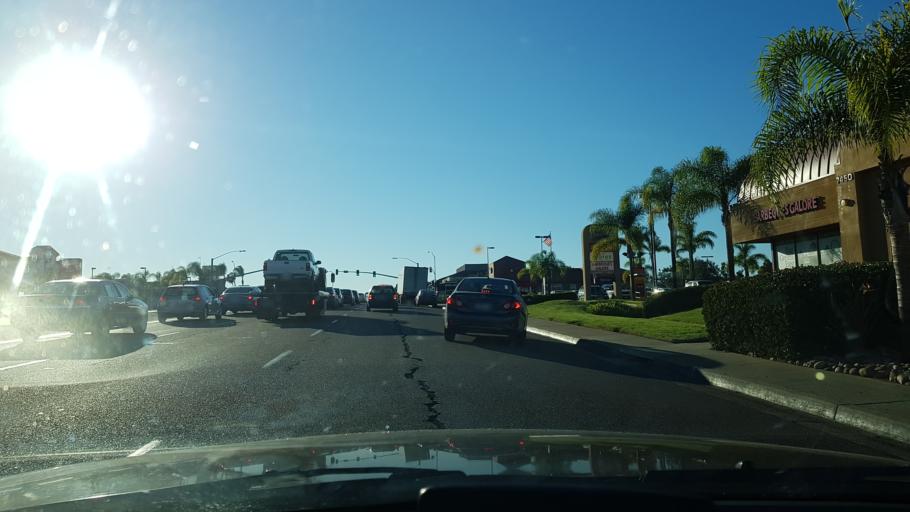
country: US
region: California
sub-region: San Diego County
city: La Jolla
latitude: 32.8329
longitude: -117.1580
